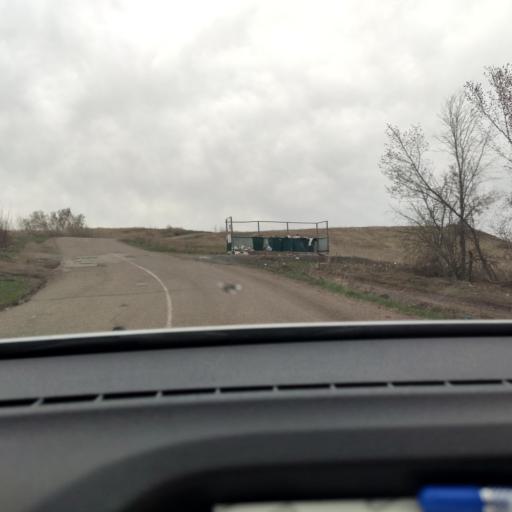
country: RU
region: Bashkortostan
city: Avdon
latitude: 54.6303
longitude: 55.5993
